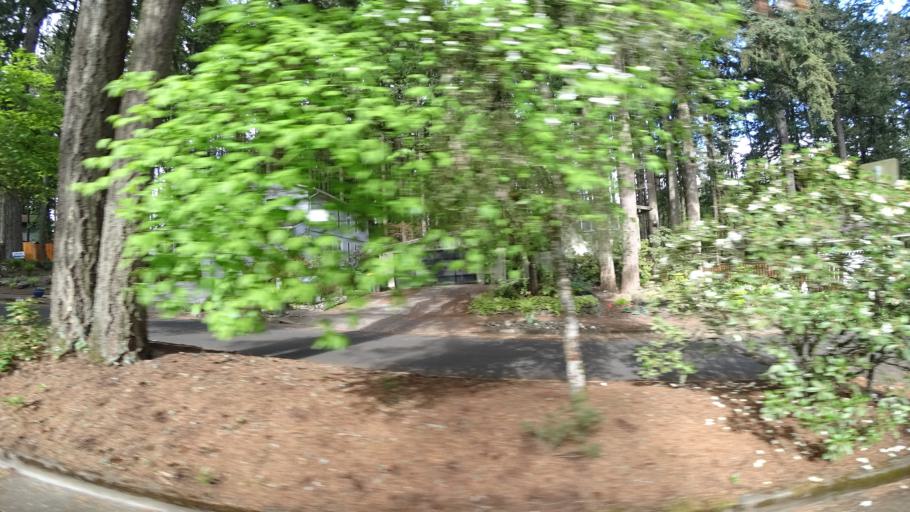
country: US
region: Oregon
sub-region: Washington County
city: Beaverton
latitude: 45.4670
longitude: -122.8293
